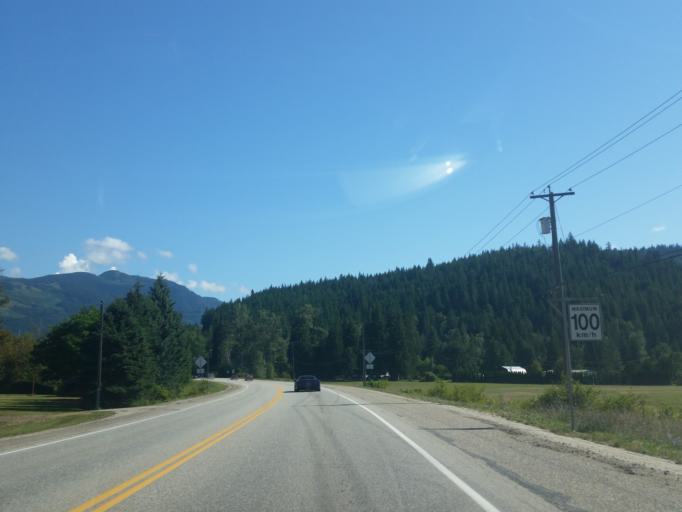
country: CA
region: British Columbia
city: Sicamous
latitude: 50.8492
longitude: -118.9484
